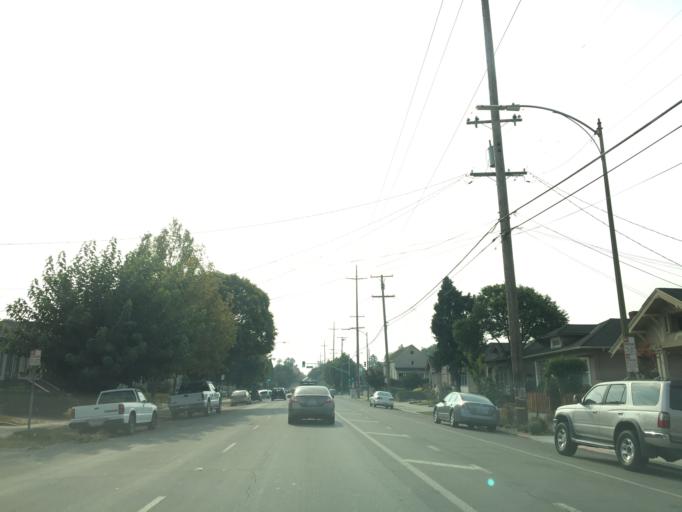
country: US
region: California
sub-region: Santa Clara County
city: San Jose
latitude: 37.3447
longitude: -121.8841
